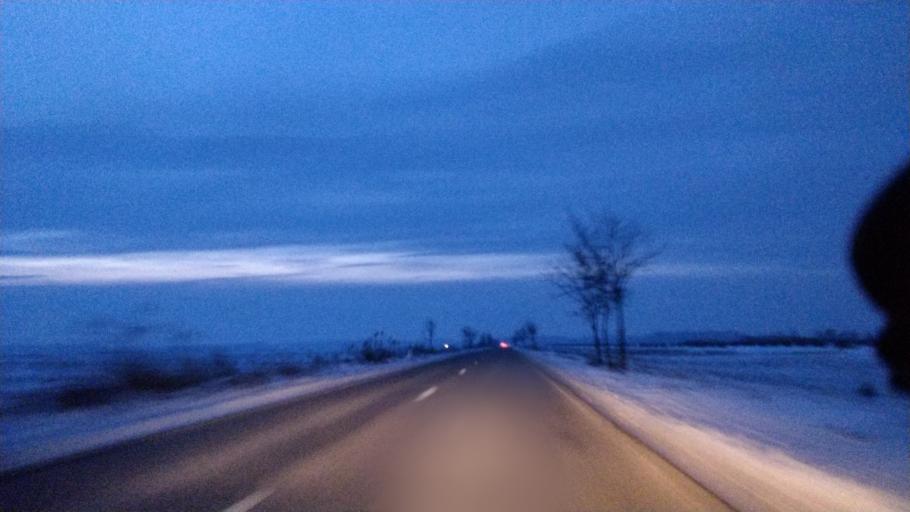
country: RO
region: Vrancea
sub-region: Comuna Suraia
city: Suraia
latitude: 45.6413
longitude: 27.3650
